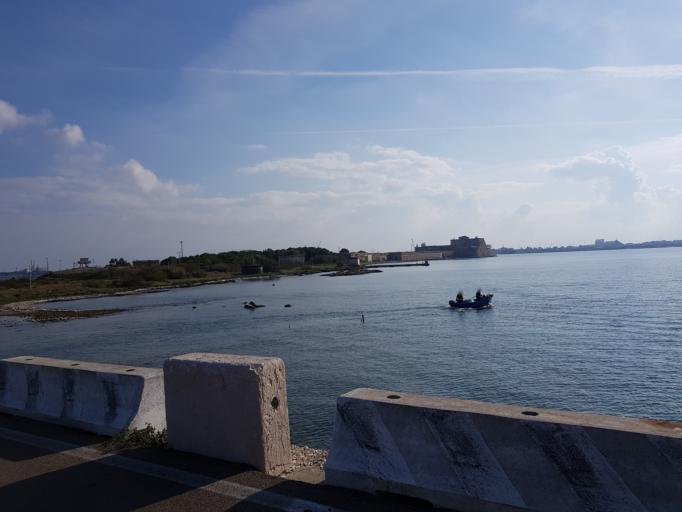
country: IT
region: Apulia
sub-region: Provincia di Brindisi
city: Materdomini
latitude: 40.6627
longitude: 17.9666
